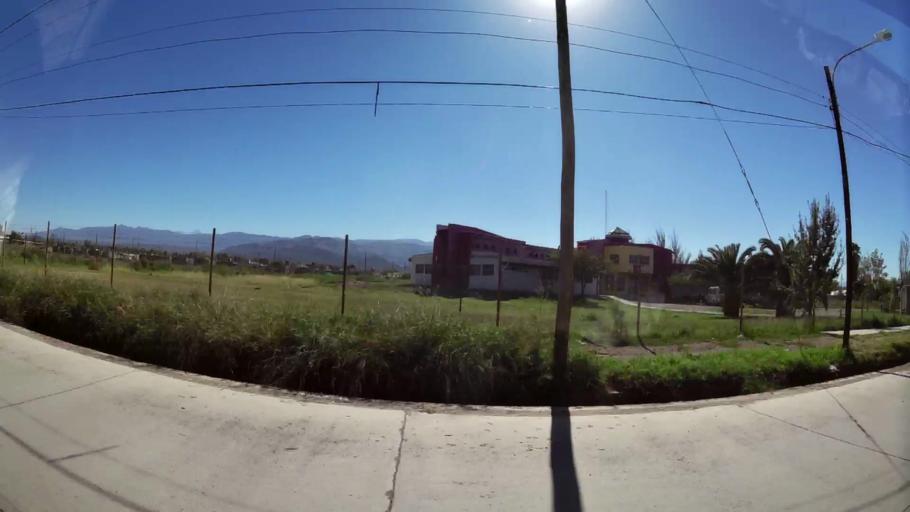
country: AR
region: Mendoza
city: Las Heras
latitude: -32.8332
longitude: -68.8153
